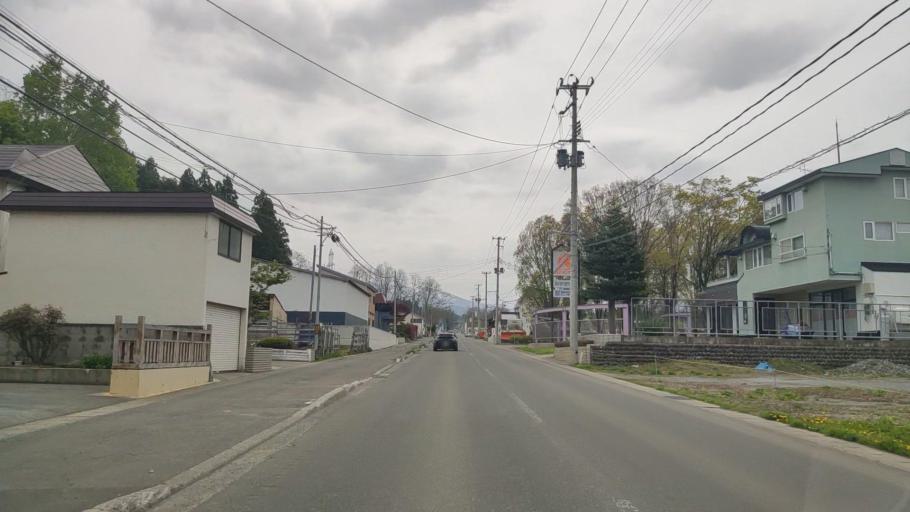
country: JP
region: Aomori
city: Aomori Shi
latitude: 40.7812
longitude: 140.7922
